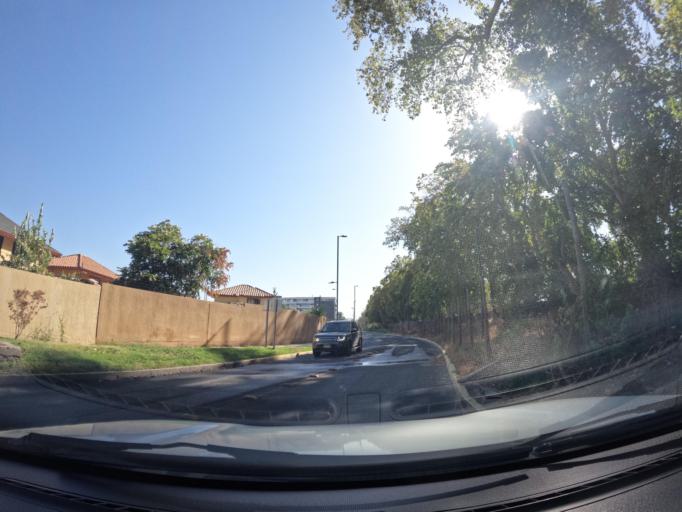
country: CL
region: Santiago Metropolitan
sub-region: Provincia de Santiago
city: Villa Presidente Frei, Nunoa, Santiago, Chile
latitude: -33.4924
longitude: -70.5690
